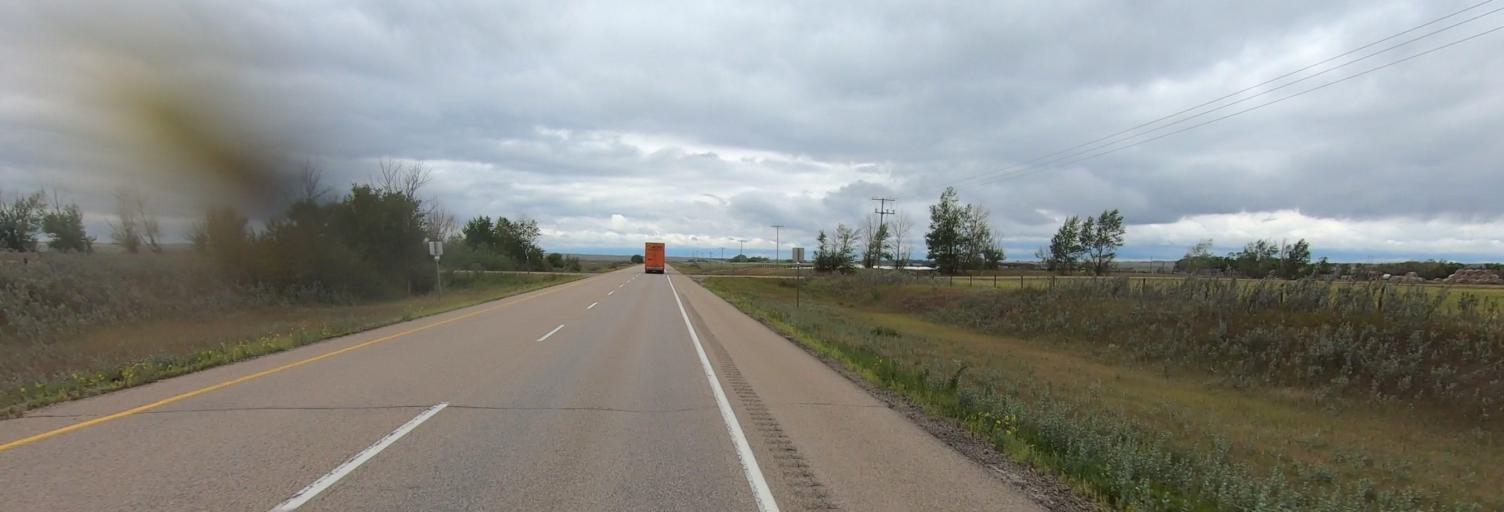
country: CA
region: Saskatchewan
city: Gravelbourg
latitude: 50.4657
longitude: -106.7356
